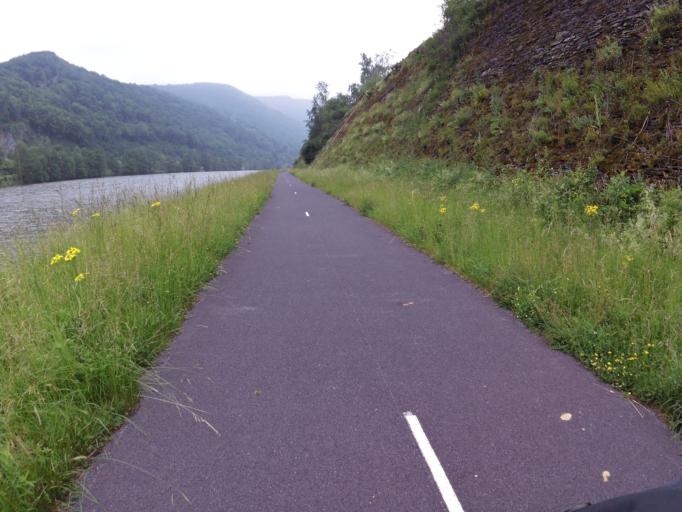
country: FR
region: Champagne-Ardenne
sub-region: Departement des Ardennes
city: Fumay
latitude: 49.9953
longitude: 4.6985
